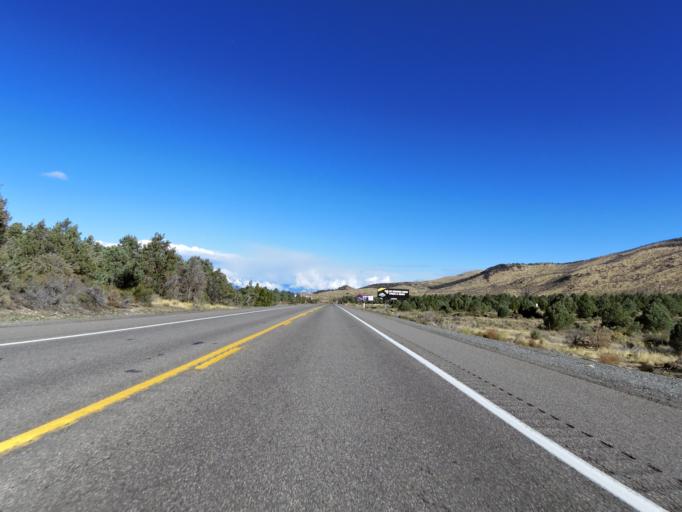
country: US
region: Nevada
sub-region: Douglas County
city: Gardnerville Ranchos
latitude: 38.8107
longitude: -119.6115
